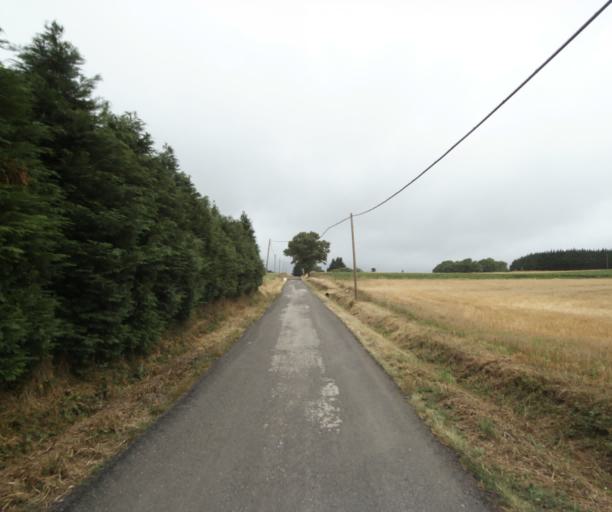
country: FR
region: Midi-Pyrenees
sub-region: Departement du Tarn
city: Soreze
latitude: 43.4070
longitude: 2.0725
